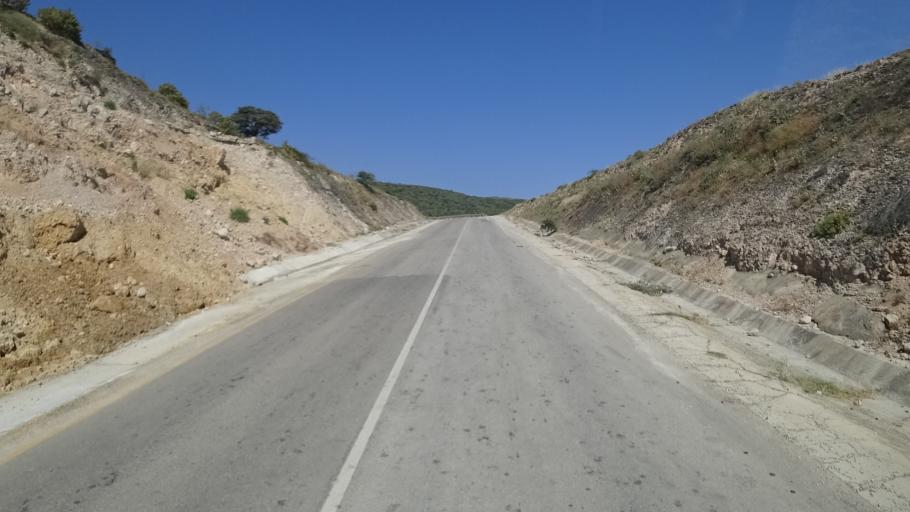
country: OM
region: Zufar
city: Salalah
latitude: 17.0487
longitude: 54.6116
